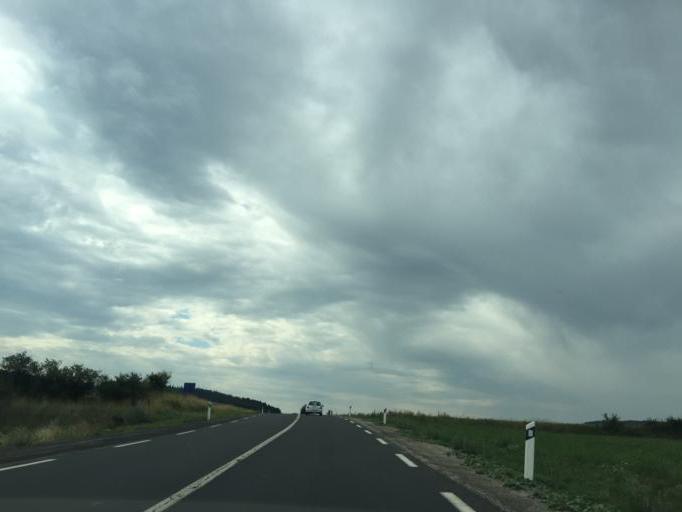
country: FR
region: Auvergne
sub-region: Departement de la Haute-Loire
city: Solignac-sur-Loire
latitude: 44.9079
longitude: 3.8497
